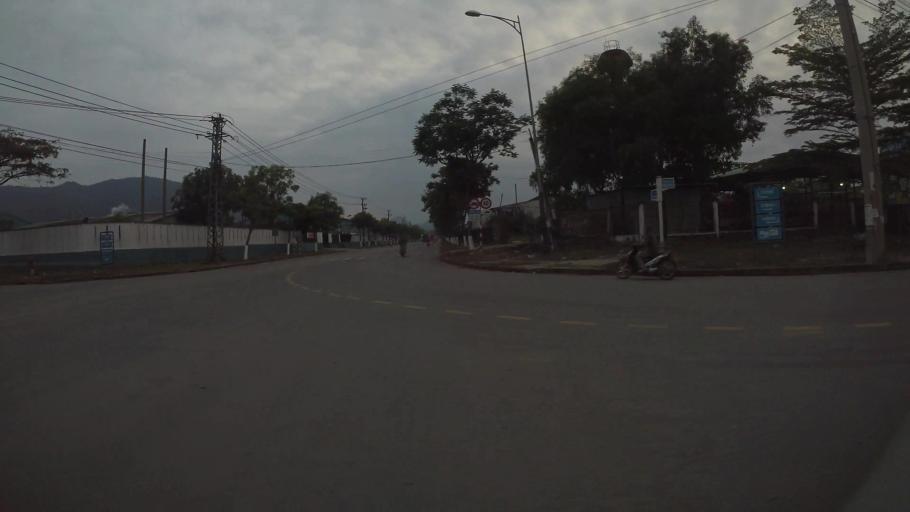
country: VN
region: Da Nang
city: Lien Chieu
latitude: 16.0826
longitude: 108.1179
